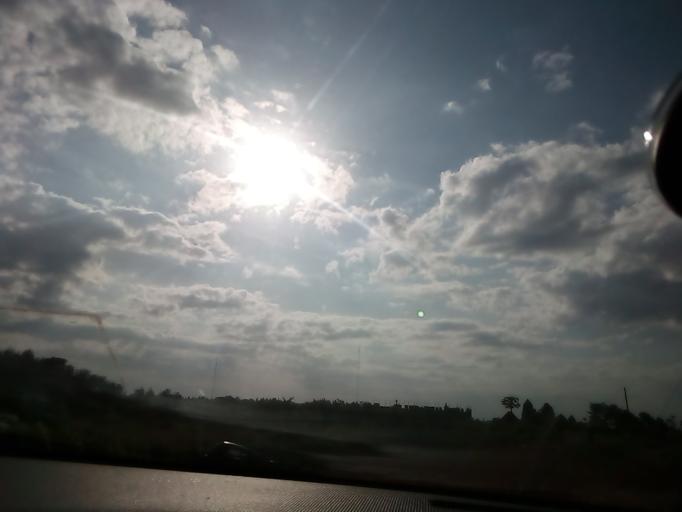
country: UG
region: Central Region
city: Masaka
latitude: -0.3618
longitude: 31.7476
